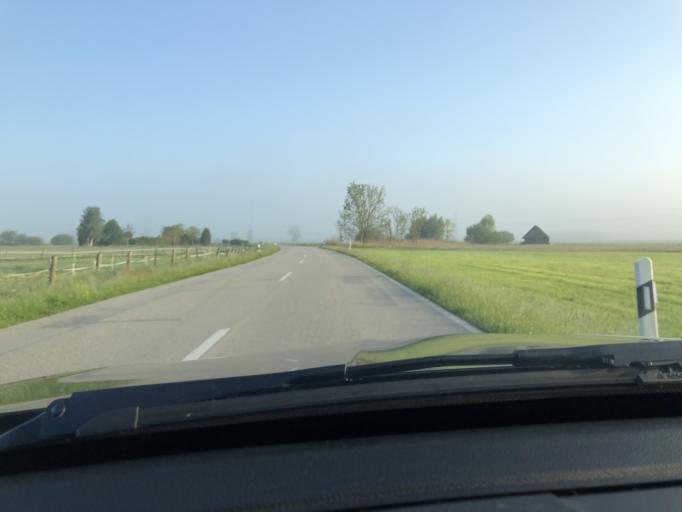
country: DE
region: Bavaria
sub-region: Upper Bavaria
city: Wolfersdorf
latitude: 48.4418
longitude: 11.7224
